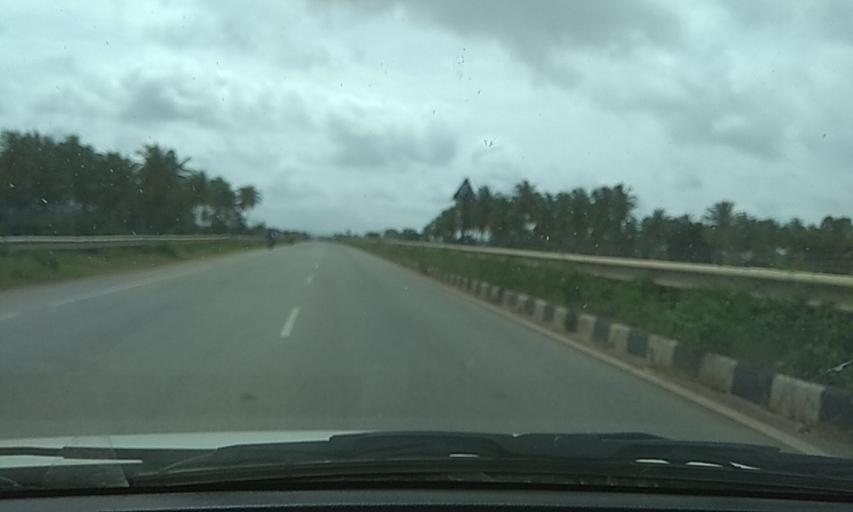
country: IN
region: Karnataka
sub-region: Davanagere
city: Harihar
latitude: 14.4518
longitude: 75.8751
